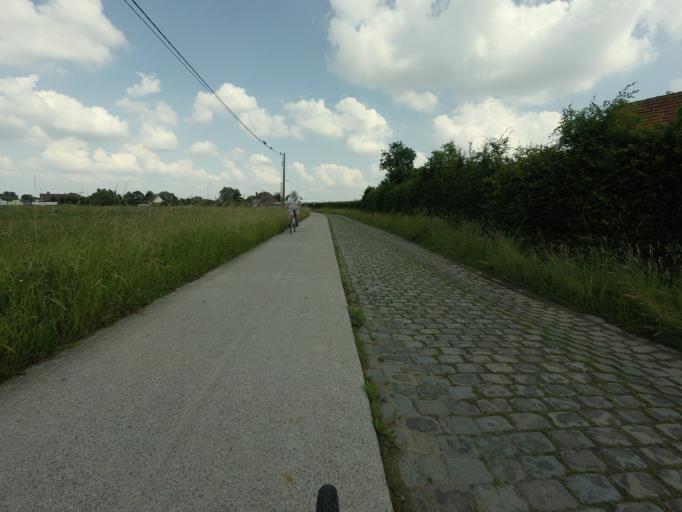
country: BE
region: Flanders
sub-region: Provincie Antwerpen
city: Lint
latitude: 51.1174
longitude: 4.5159
